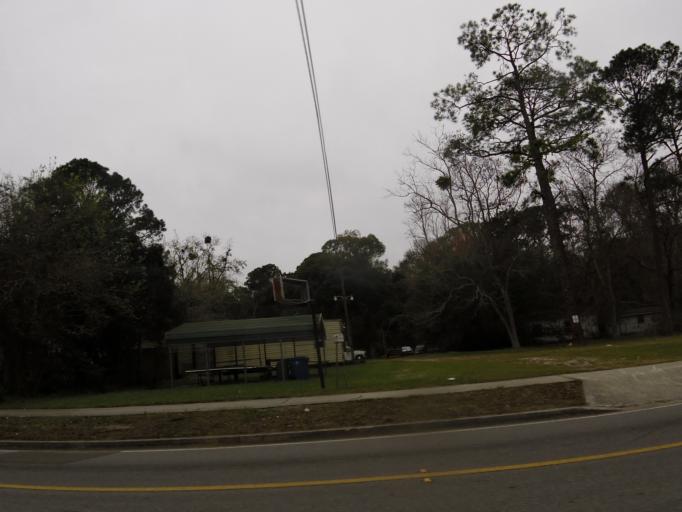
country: US
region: Florida
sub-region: Duval County
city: Jacksonville
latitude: 30.3725
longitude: -81.6990
